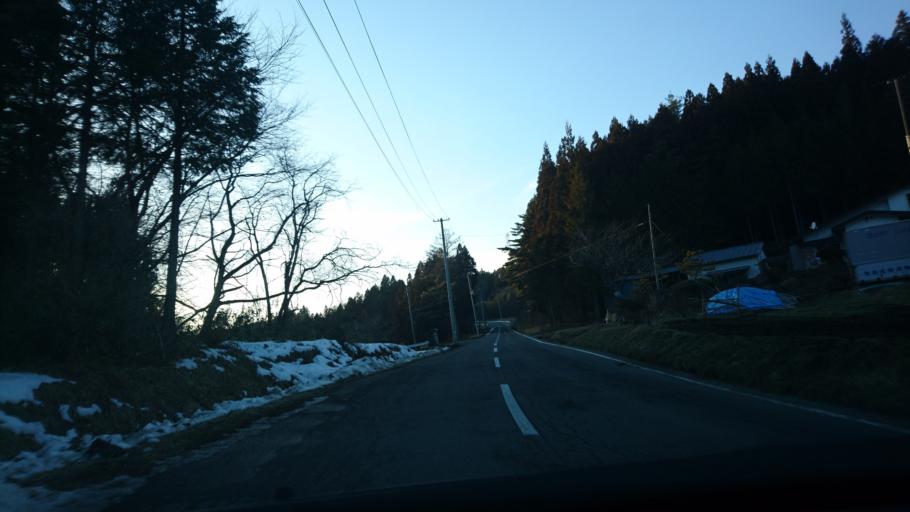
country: JP
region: Iwate
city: Mizusawa
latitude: 39.0386
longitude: 141.3233
